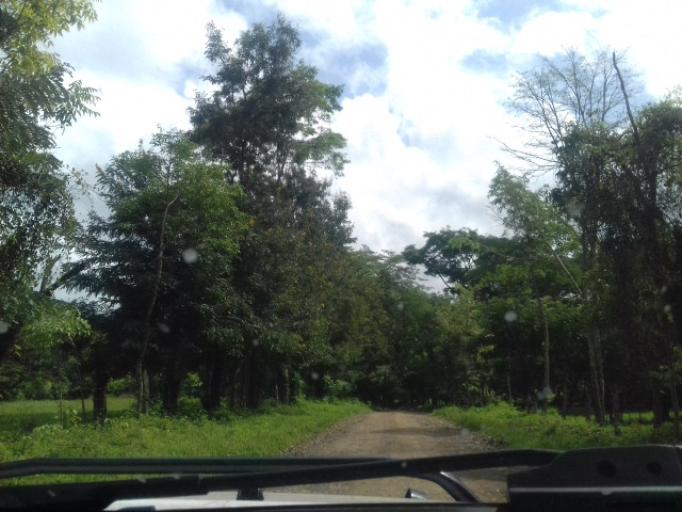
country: NI
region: Matagalpa
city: Matiguas
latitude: 12.8668
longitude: -85.3864
